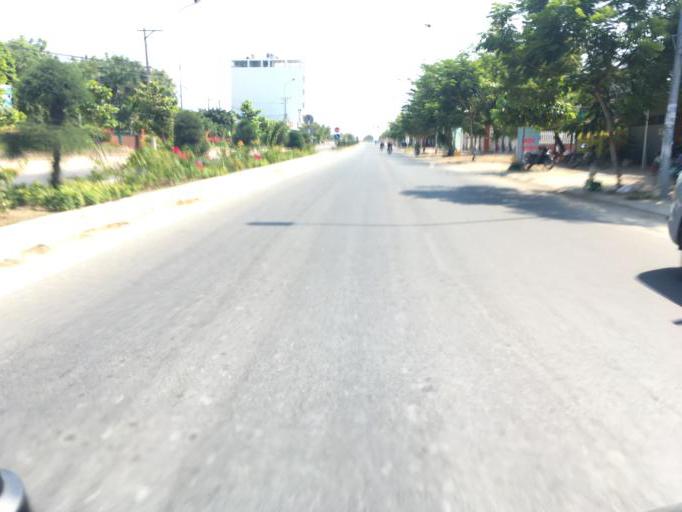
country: VN
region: Ninh Thuan
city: Phan Rang-Thap Cham
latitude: 11.5620
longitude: 109.0215
